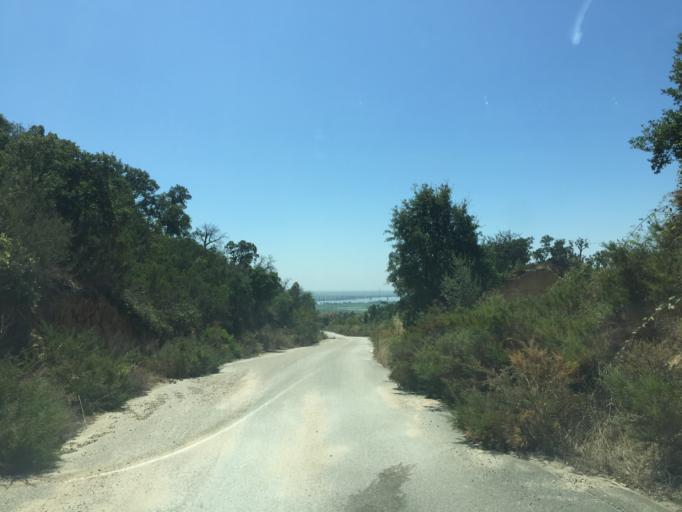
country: PT
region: Lisbon
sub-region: Alenquer
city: Carregado
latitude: 39.0517
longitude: -8.9267
